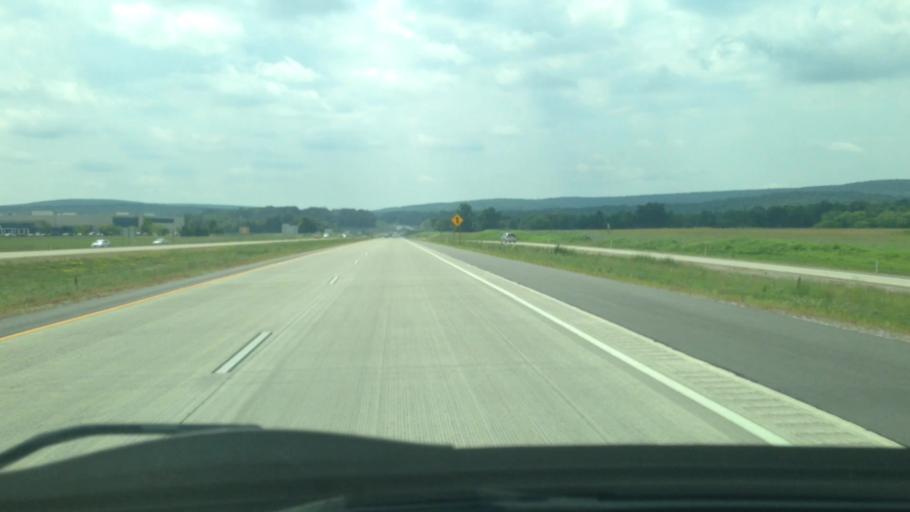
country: US
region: Wisconsin
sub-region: Sauk County
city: West Baraboo
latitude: 43.4588
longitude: -89.7783
